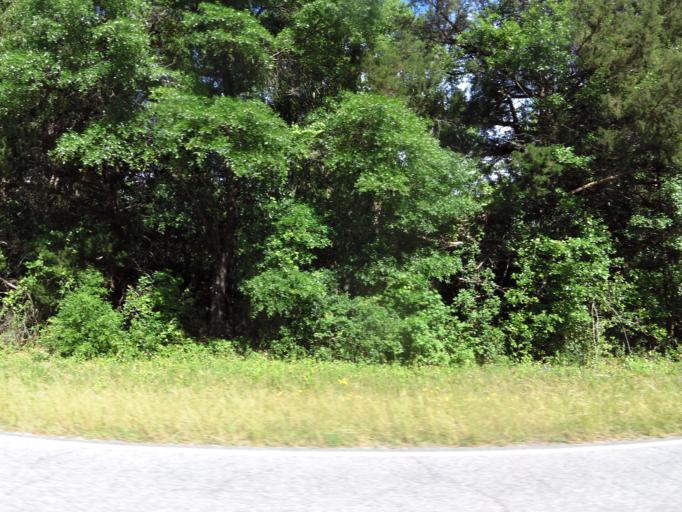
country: US
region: South Carolina
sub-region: Bamberg County
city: Denmark
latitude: 33.1734
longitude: -81.1874
